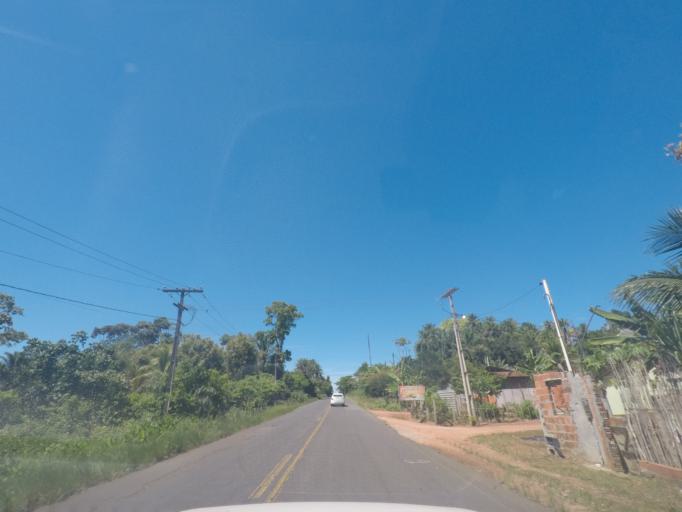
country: BR
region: Bahia
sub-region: Taperoa
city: Taperoa
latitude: -13.4543
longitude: -39.0873
